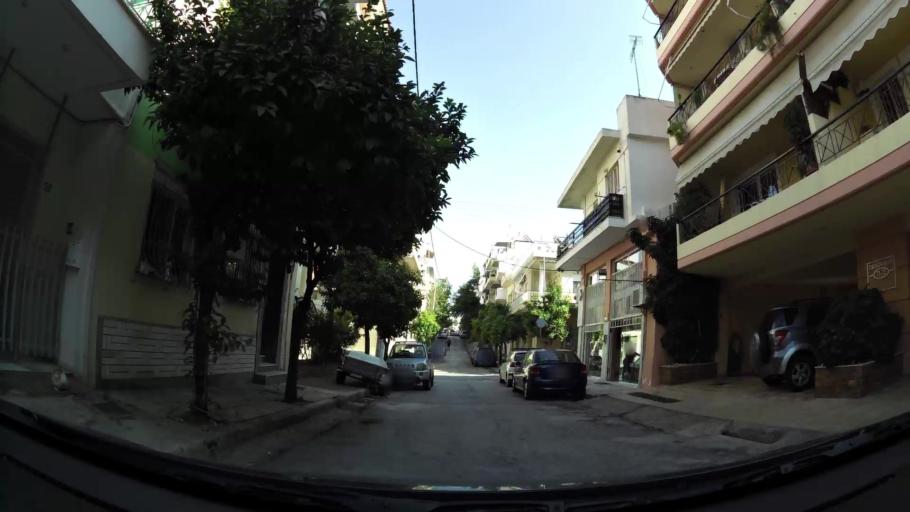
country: GR
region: Attica
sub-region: Nomos Piraios
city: Keratsini
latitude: 37.9581
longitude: 23.6200
